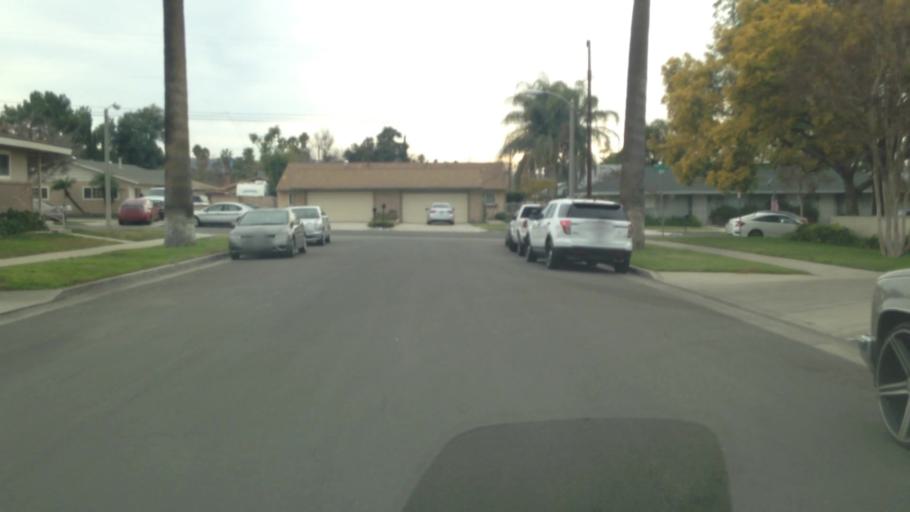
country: US
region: California
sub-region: Riverside County
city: Riverside
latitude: 33.9221
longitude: -117.4379
